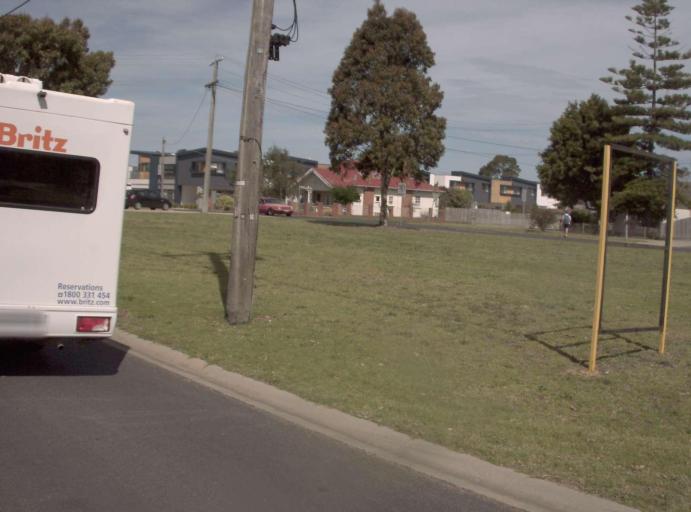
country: AU
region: Victoria
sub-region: East Gippsland
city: Bairnsdale
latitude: -37.8293
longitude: 147.6149
